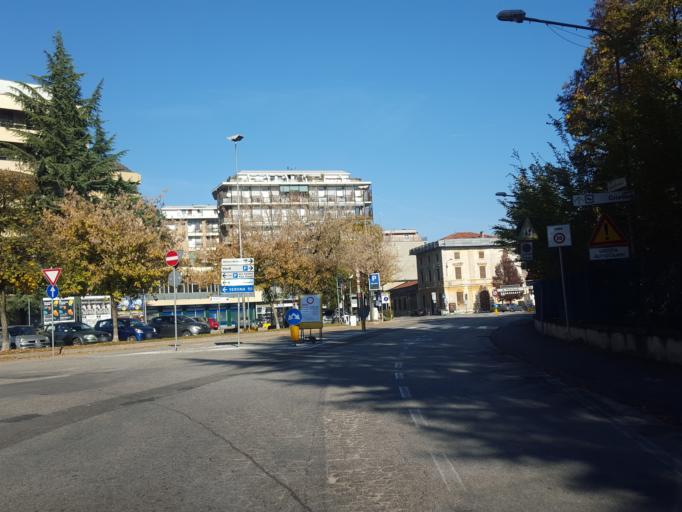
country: IT
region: Veneto
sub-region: Provincia di Vicenza
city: Vicenza
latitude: 45.5433
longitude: 11.5375
